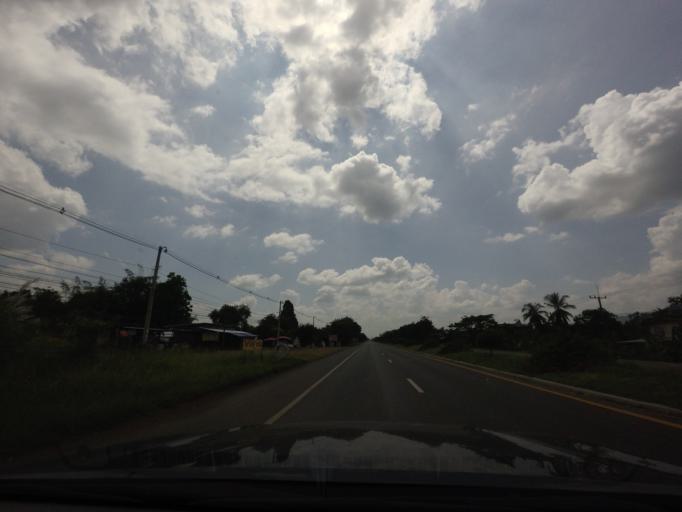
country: TH
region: Phetchabun
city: Nong Phai
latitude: 16.1718
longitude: 101.0786
